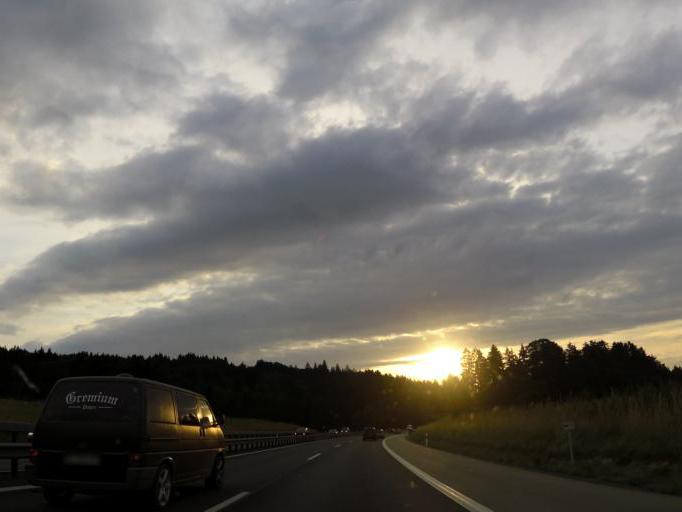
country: DE
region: Bavaria
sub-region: Upper Bavaria
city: Inzell
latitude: 47.8266
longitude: 12.7542
